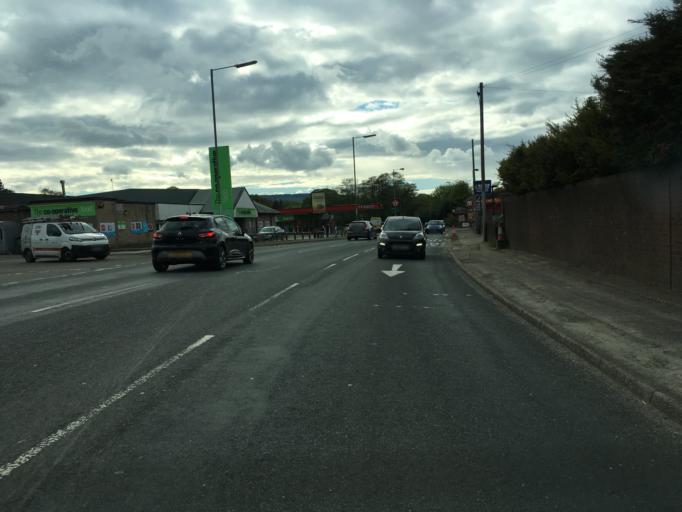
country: GB
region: Wales
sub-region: Caerphilly County Borough
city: Nelson
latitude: 51.6475
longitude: -3.2899
